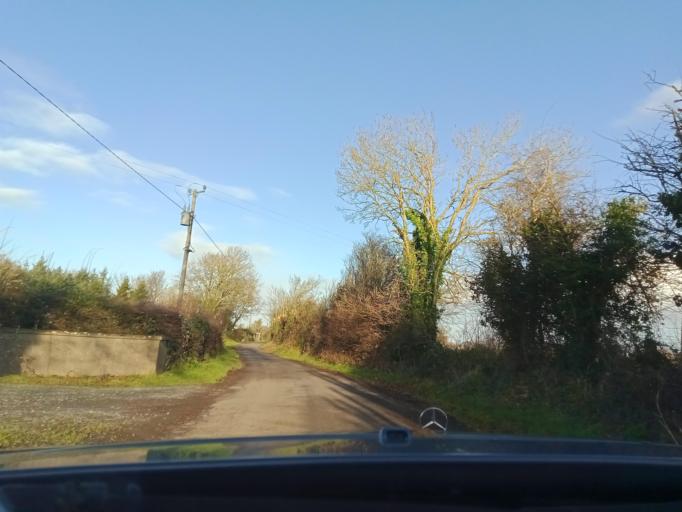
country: IE
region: Leinster
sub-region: Kilkenny
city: Callan
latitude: 52.4954
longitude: -7.3568
